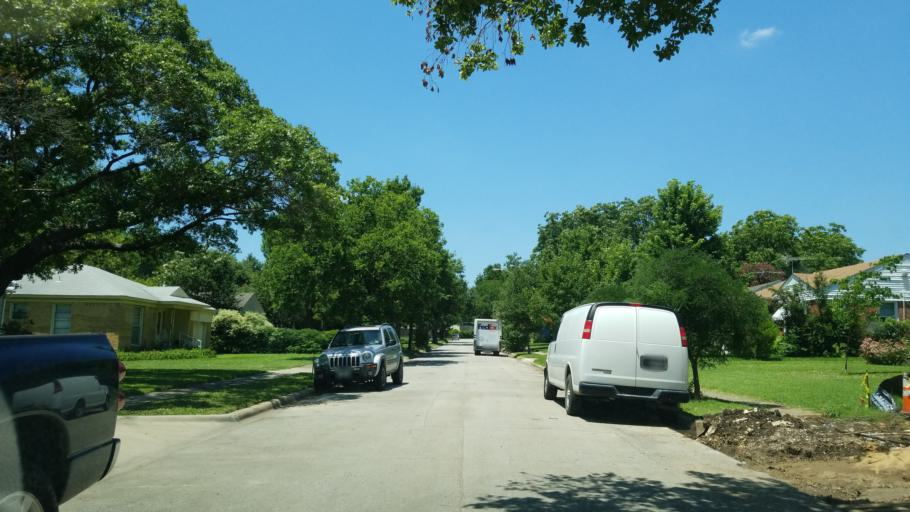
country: US
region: Texas
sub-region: Dallas County
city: University Park
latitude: 32.8784
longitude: -96.8496
